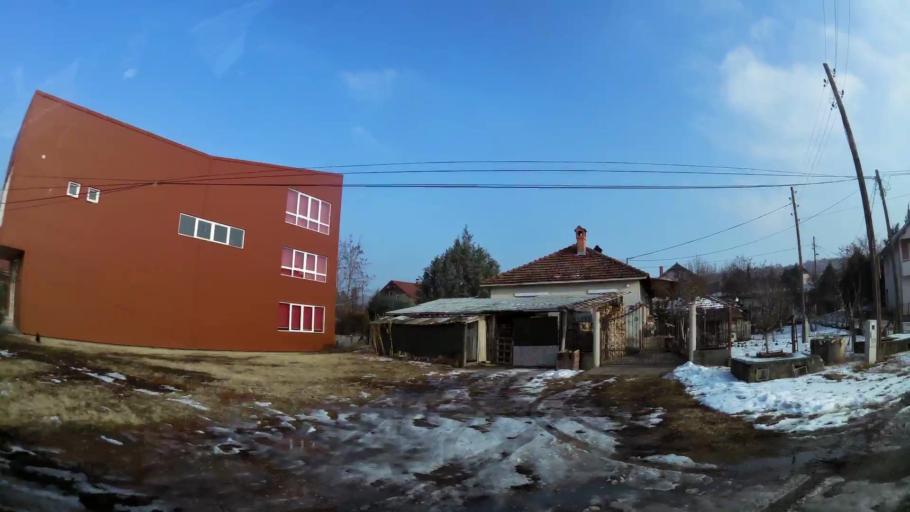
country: MK
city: Miladinovci
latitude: 41.9783
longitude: 21.6498
